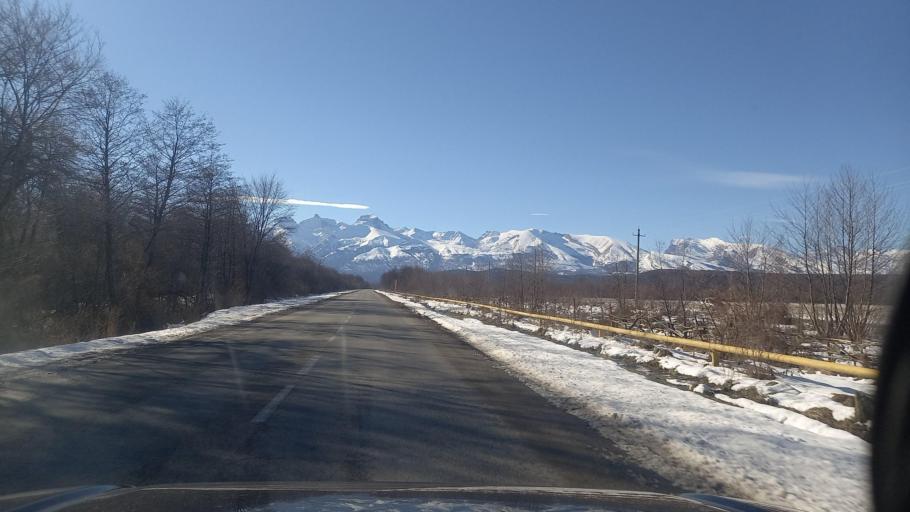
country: RU
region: North Ossetia
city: Chikola
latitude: 43.1586
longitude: 43.8479
